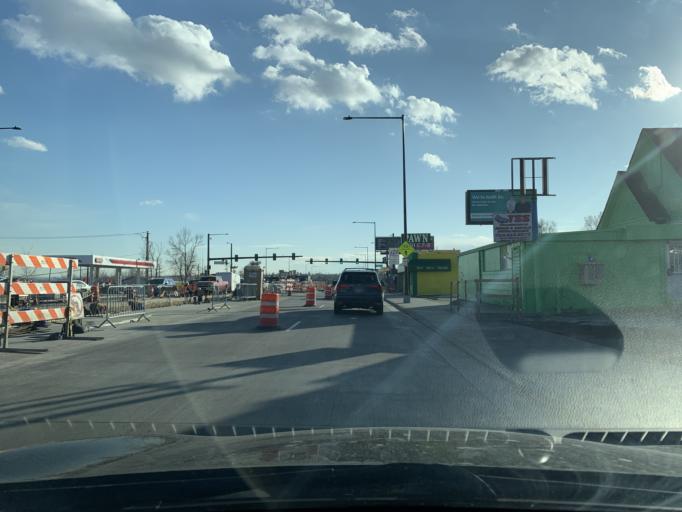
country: US
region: Colorado
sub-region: Denver County
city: Denver
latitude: 39.7340
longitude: -105.0253
